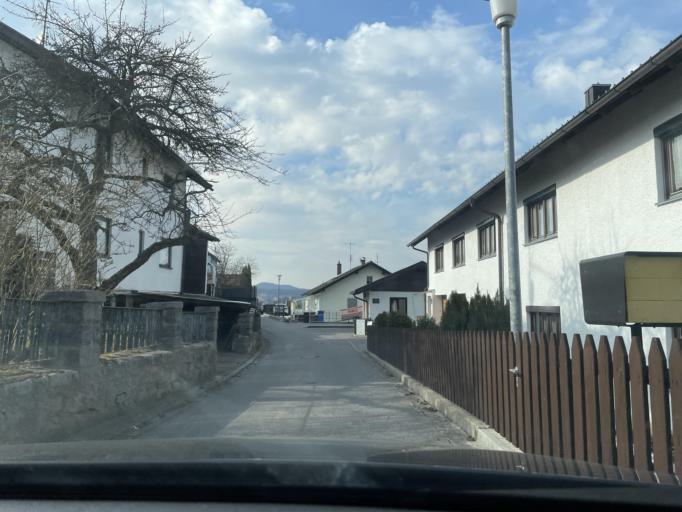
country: DE
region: Bavaria
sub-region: Lower Bavaria
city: Viechtach
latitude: 49.0819
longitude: 12.8968
